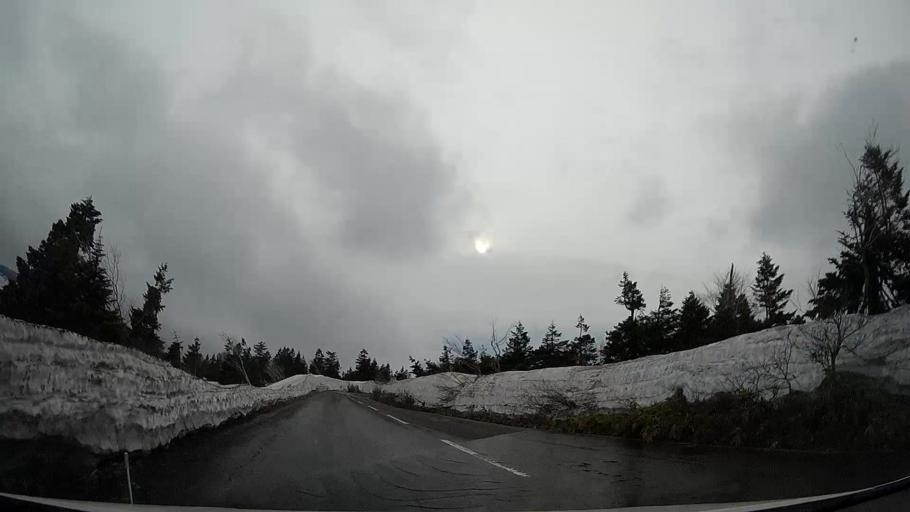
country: JP
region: Aomori
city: Aomori Shi
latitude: 40.6330
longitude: 140.8866
